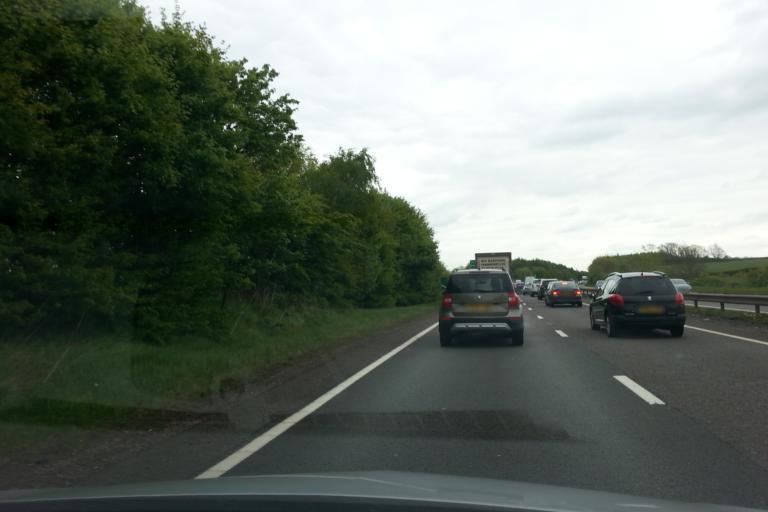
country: GB
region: England
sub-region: Derbyshire
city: Melbourne
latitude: 52.7989
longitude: -1.3806
